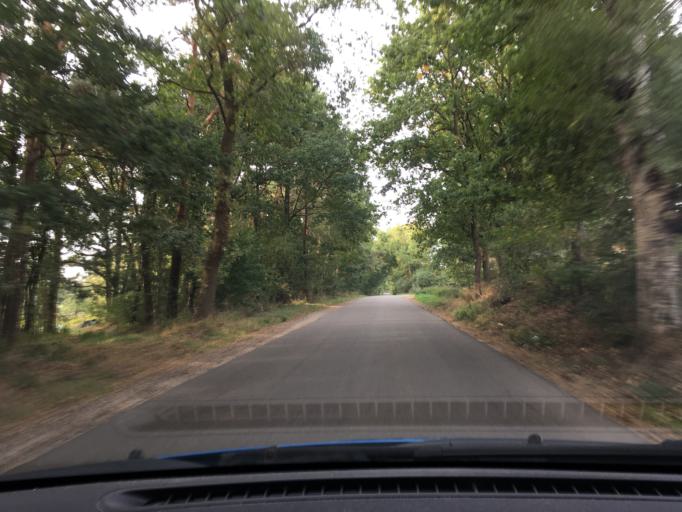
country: DE
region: Lower Saxony
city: Toppenstedt
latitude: 53.3048
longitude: 10.0961
